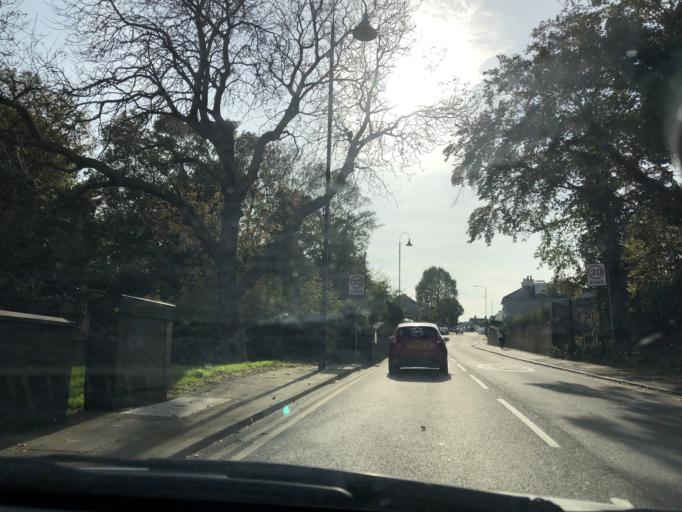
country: GB
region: England
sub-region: Greater London
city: Bexley
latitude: 51.4494
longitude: 0.1816
